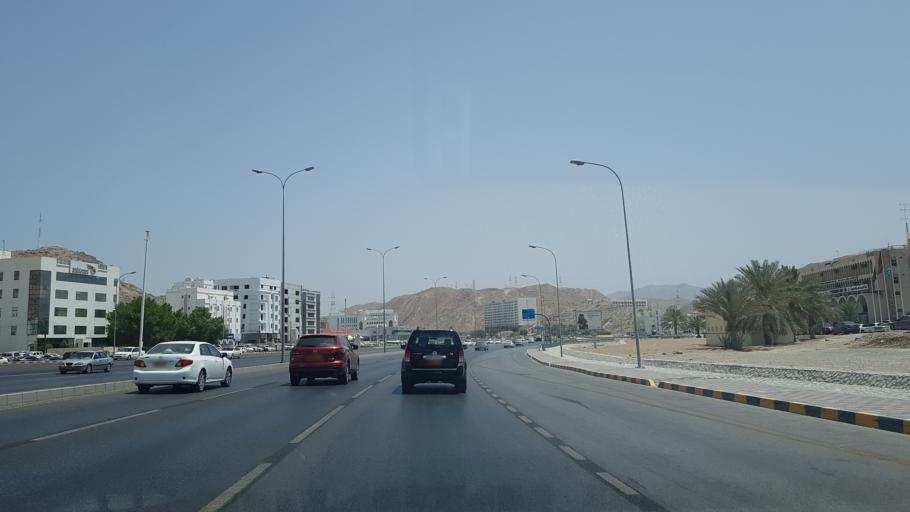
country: OM
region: Muhafazat Masqat
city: Muscat
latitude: 23.5991
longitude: 58.5191
